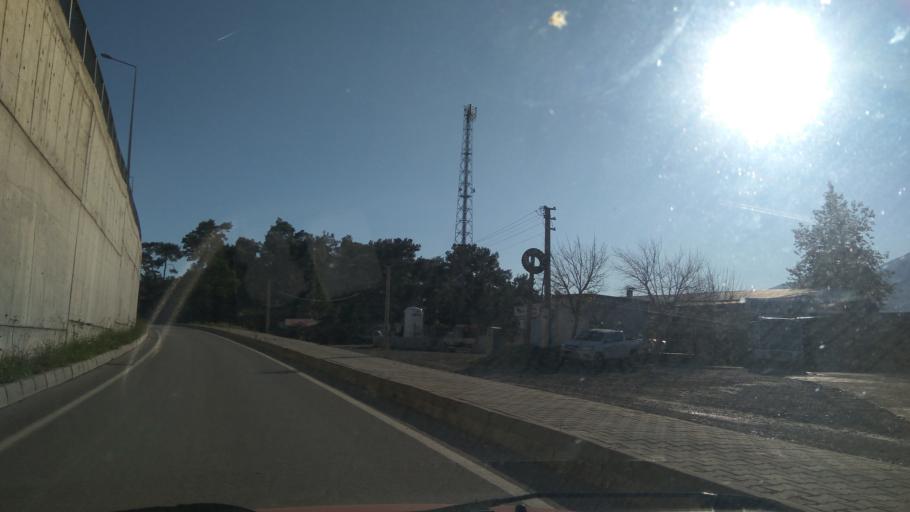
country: TR
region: Antalya
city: Kemer
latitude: 36.5911
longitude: 30.5405
